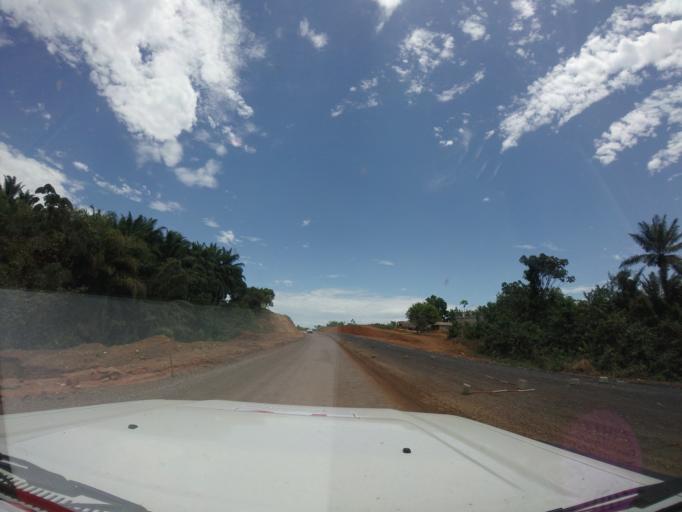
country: LR
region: Margibi
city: Kakata
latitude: 6.7512
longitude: -10.0858
